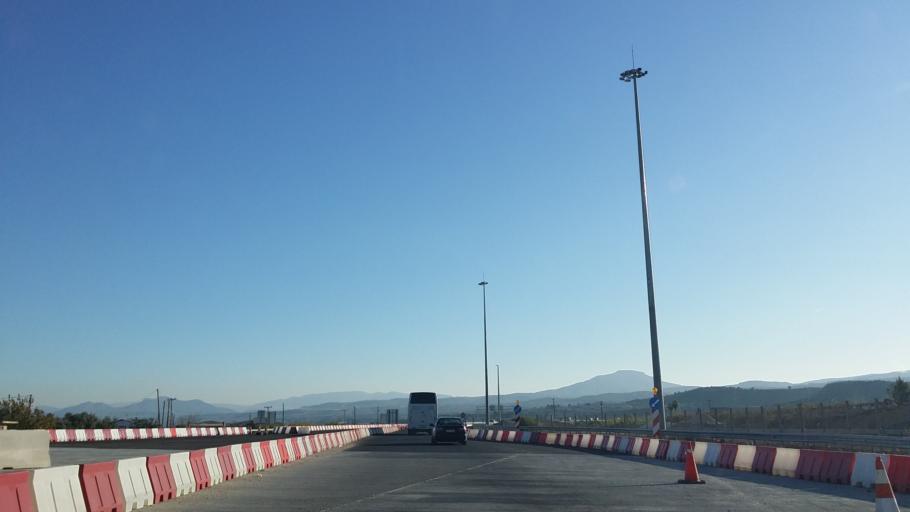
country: GR
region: Peloponnese
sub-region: Nomos Korinthias
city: Moulki
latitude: 37.9961
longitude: 22.7351
